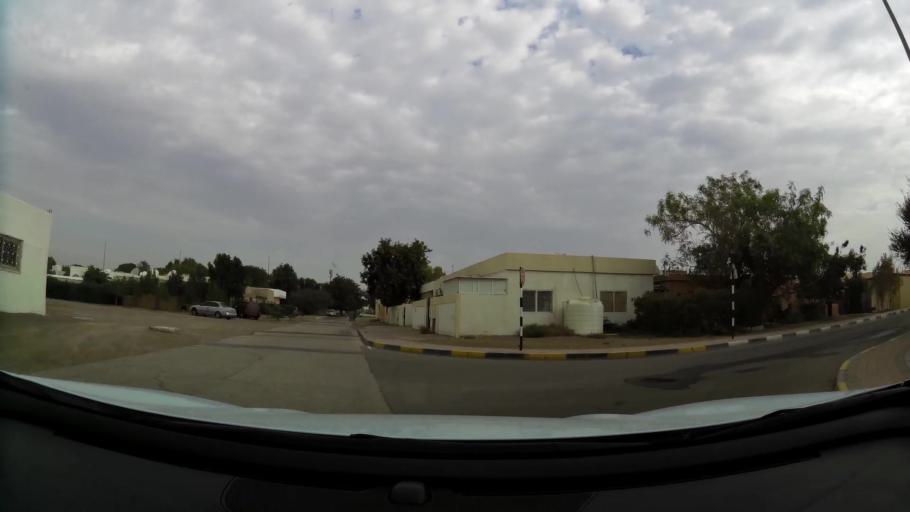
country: AE
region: Abu Dhabi
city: Al Ain
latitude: 24.2233
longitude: 55.7331
